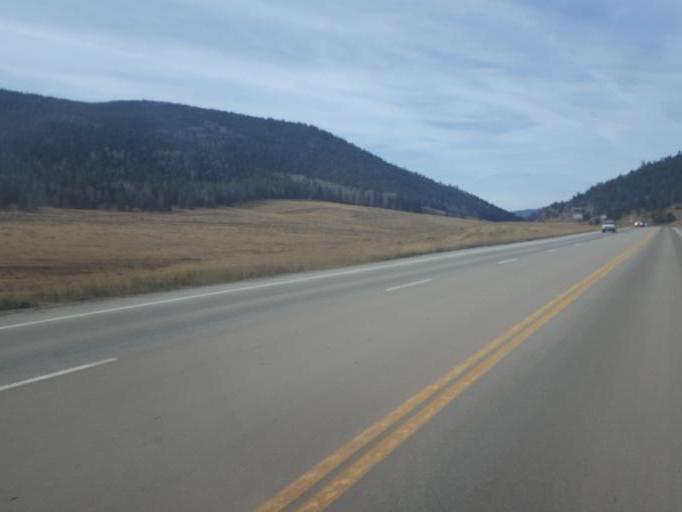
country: US
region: Colorado
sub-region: Huerfano County
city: Walsenburg
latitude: 37.6081
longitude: -105.2214
